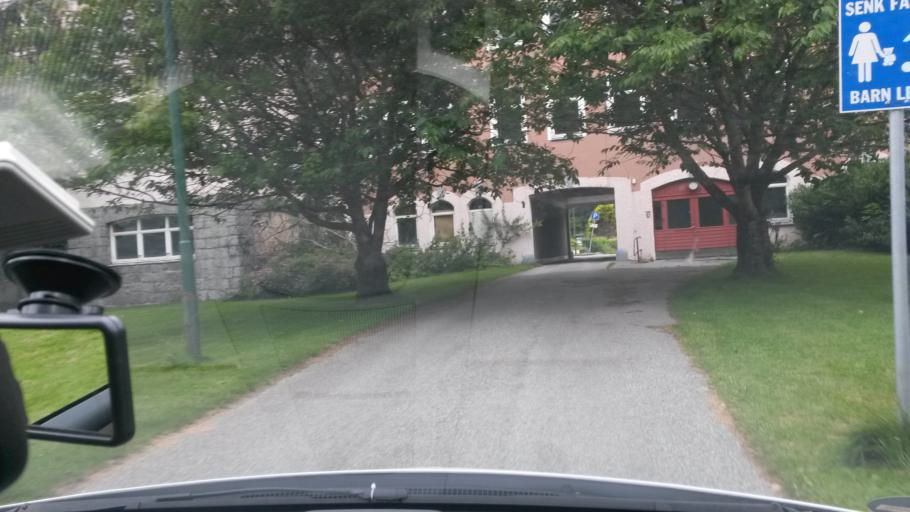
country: NO
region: Rogaland
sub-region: Sandnes
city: Sandnes
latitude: 58.9002
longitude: 5.7801
